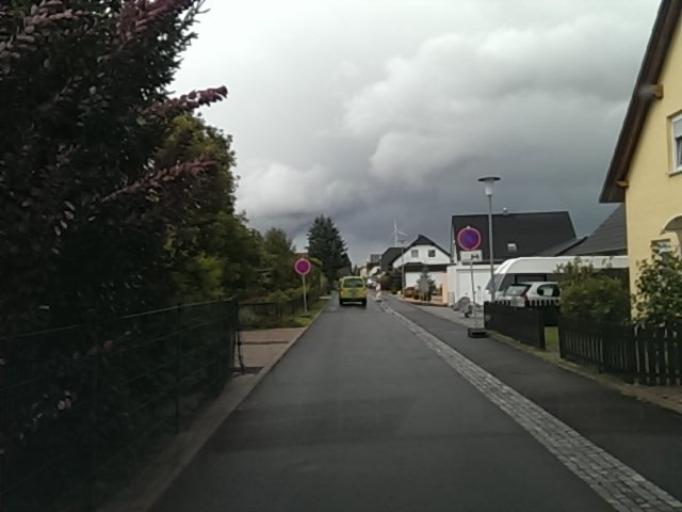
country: DE
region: Thuringia
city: Haina
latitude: 51.0221
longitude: 10.5210
